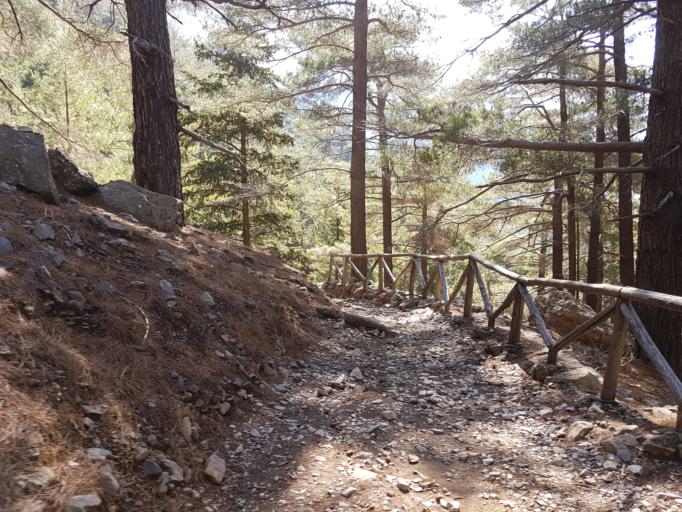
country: GR
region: Crete
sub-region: Nomos Chanias
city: Perivolia
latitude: 35.3071
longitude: 23.9270
